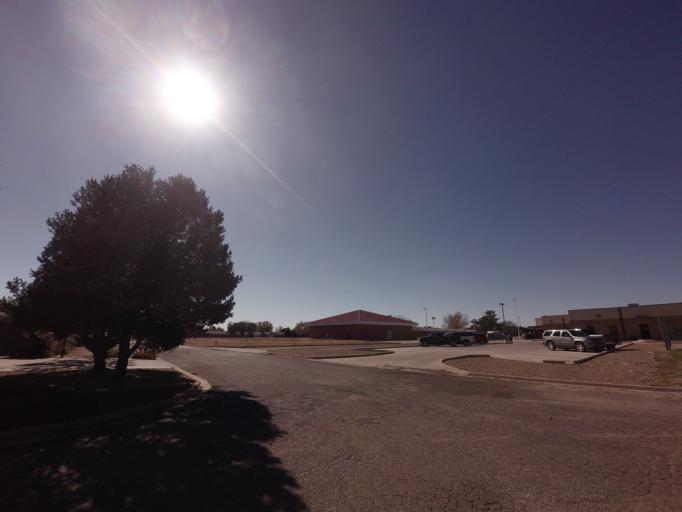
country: US
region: New Mexico
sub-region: Curry County
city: Clovis
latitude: 34.4234
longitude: -103.1925
